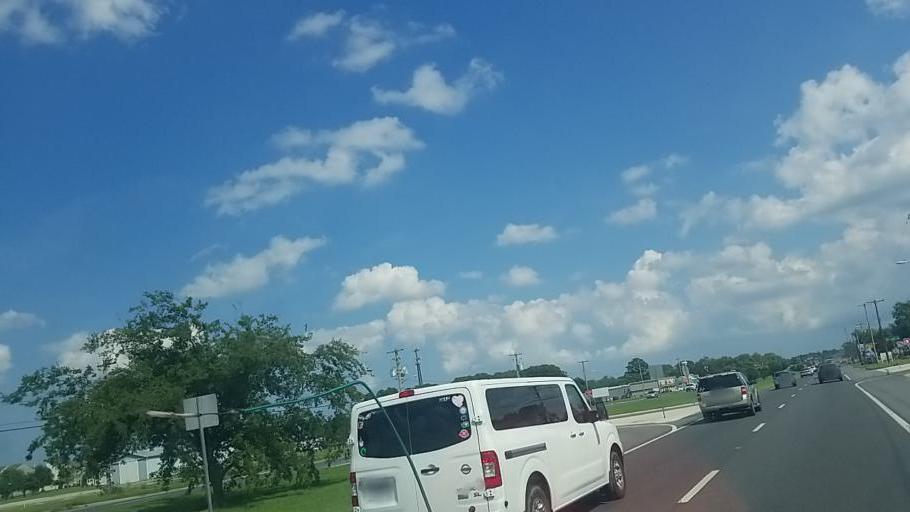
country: US
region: Delaware
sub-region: Sussex County
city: Millsboro
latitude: 38.5900
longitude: -75.3033
